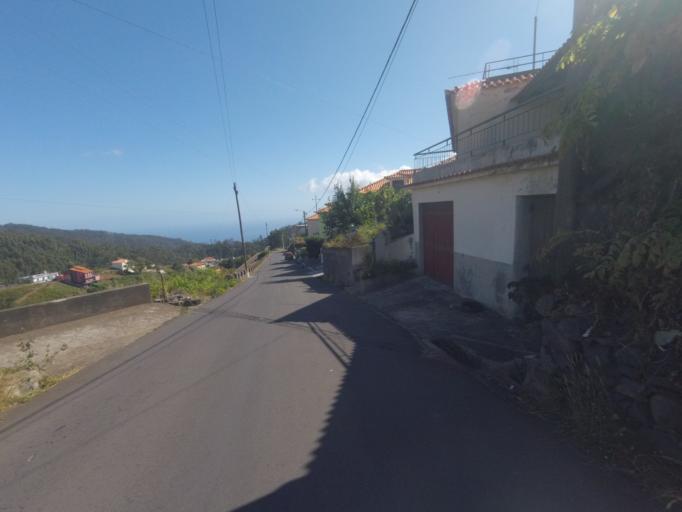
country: PT
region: Madeira
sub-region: Ribeira Brava
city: Campanario
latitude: 32.6967
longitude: -17.0267
